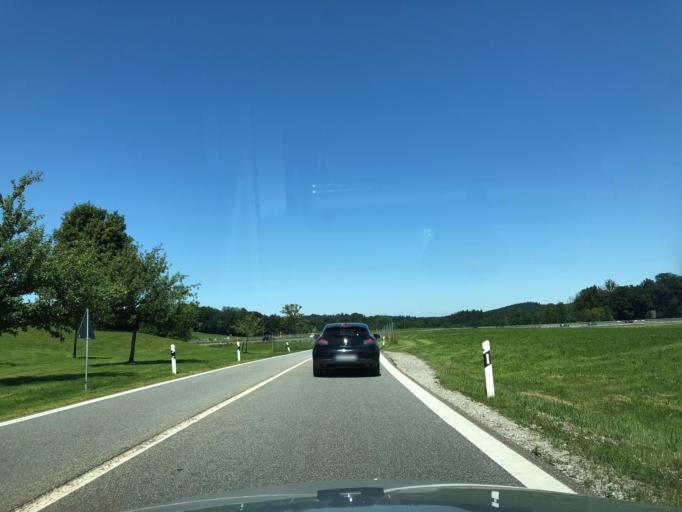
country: DE
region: Bavaria
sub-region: Upper Bavaria
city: Frasdorf
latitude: 47.8018
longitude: 12.2928
